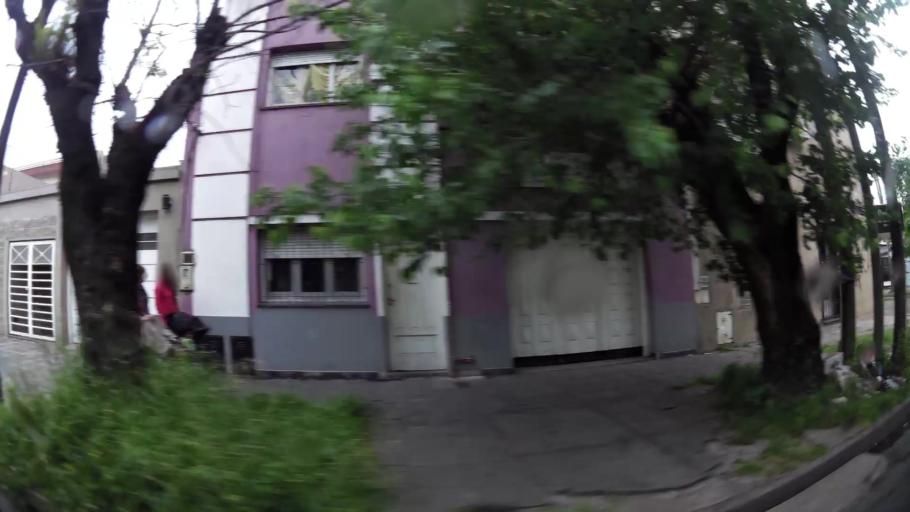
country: AR
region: Buenos Aires
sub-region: Partido de Lanus
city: Lanus
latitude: -34.6952
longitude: -58.4011
